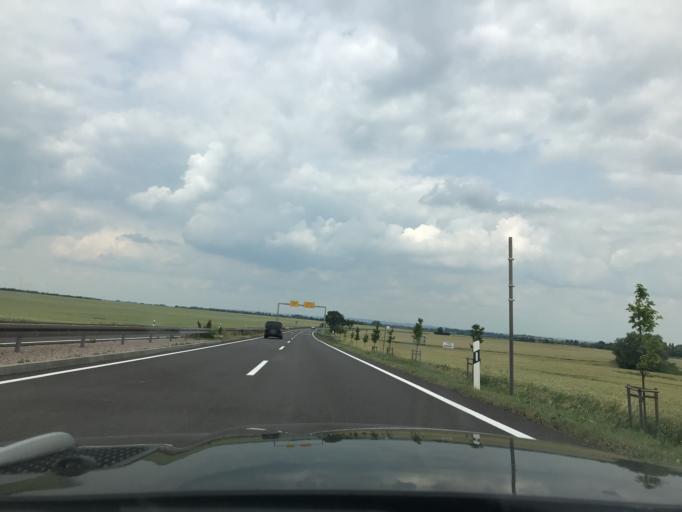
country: DE
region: Thuringia
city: Walschleben
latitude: 51.0705
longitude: 10.9262
